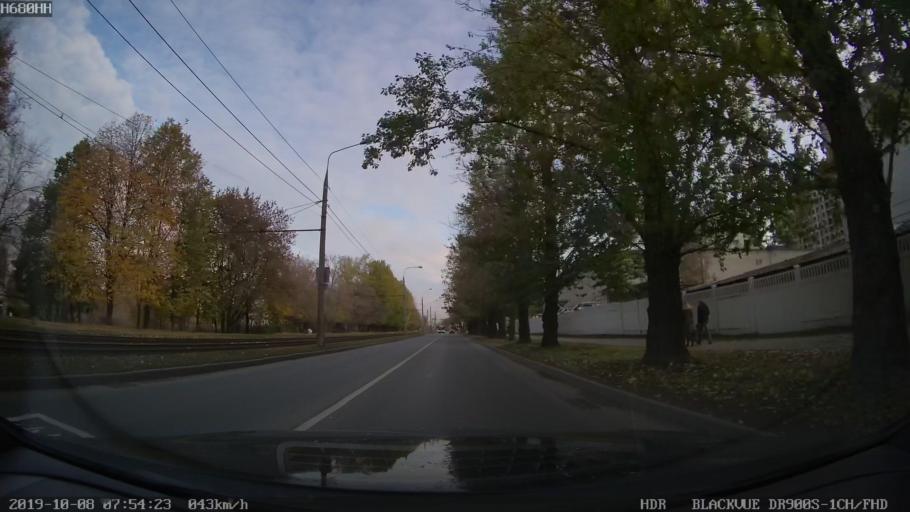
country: RU
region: Moscow
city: Shchukino
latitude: 55.7901
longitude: 37.4544
